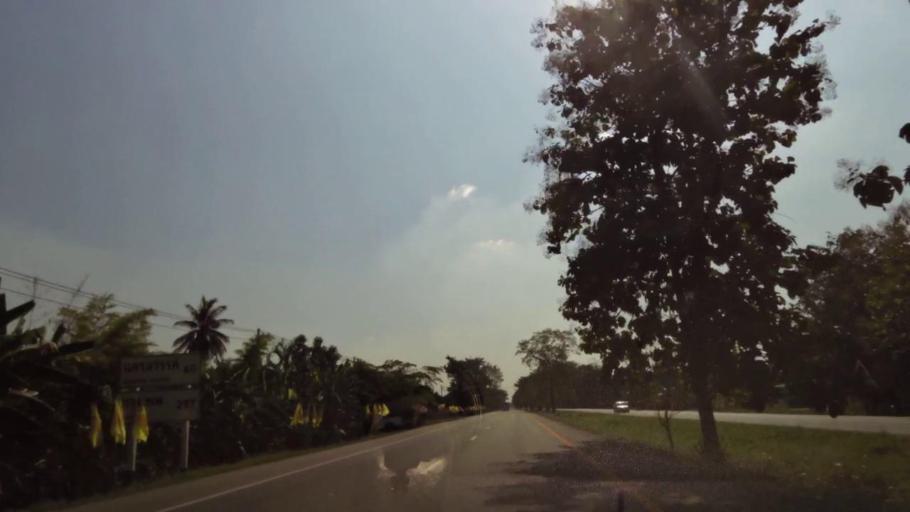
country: TH
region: Phichit
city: Bueng Na Rang
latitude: 16.2340
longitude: 100.1256
